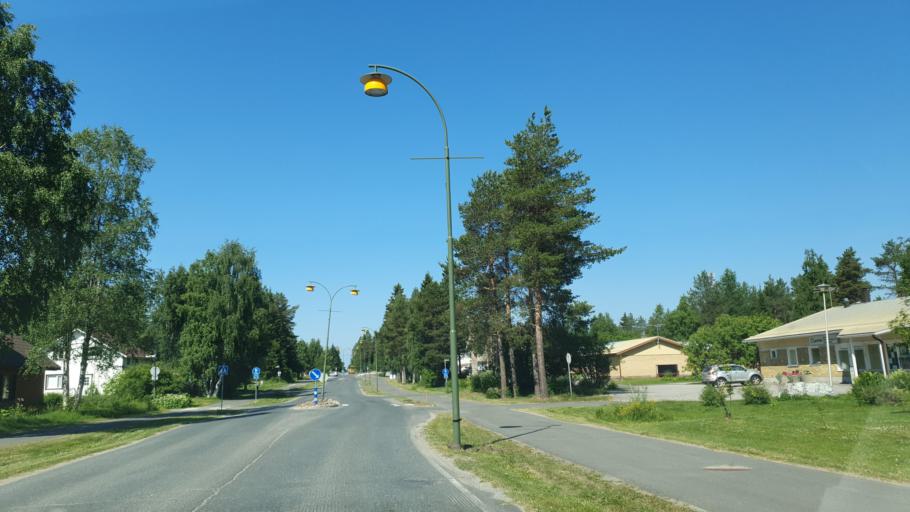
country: FI
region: Lapland
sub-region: Rovaniemi
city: Ranua
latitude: 65.9314
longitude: 26.5136
